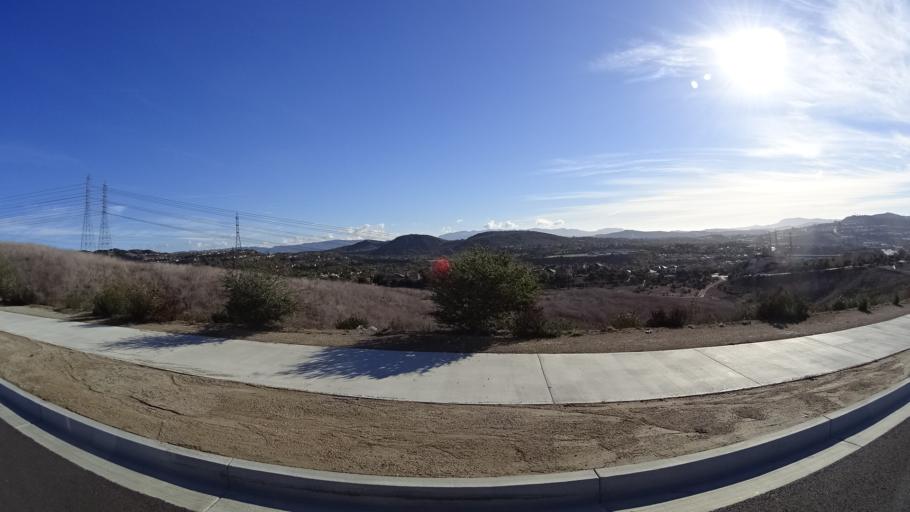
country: US
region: California
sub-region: Orange County
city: San Clemente
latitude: 33.4728
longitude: -117.6101
